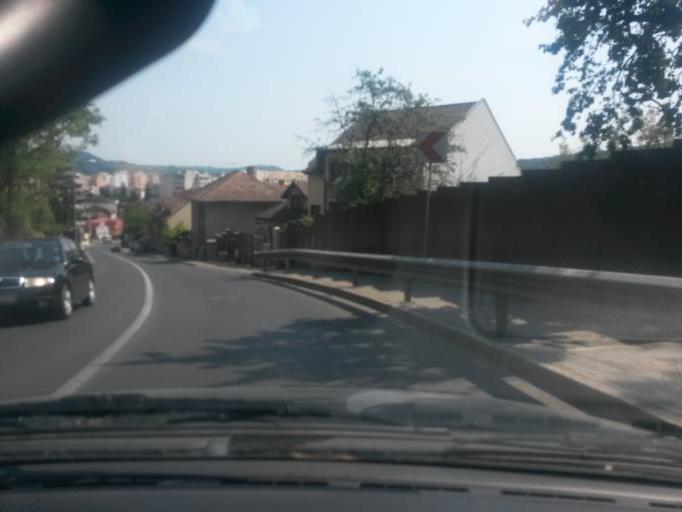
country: RO
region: Mures
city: Targu-Mures
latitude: 46.5401
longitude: 24.5740
